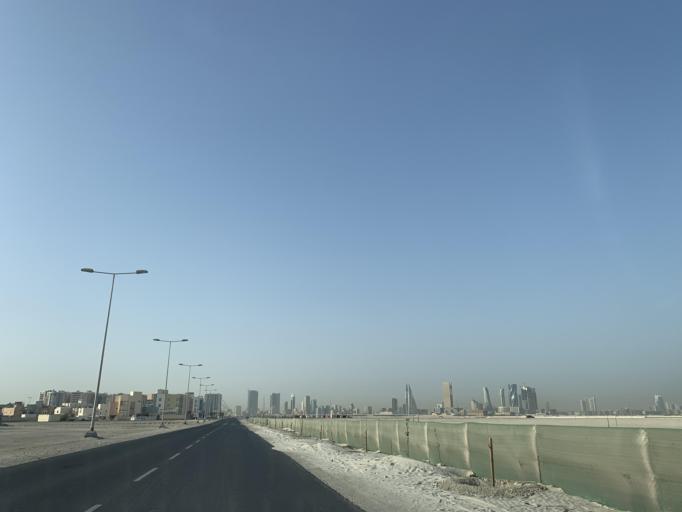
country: BH
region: Muharraq
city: Al Muharraq
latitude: 26.2754
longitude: 50.5944
